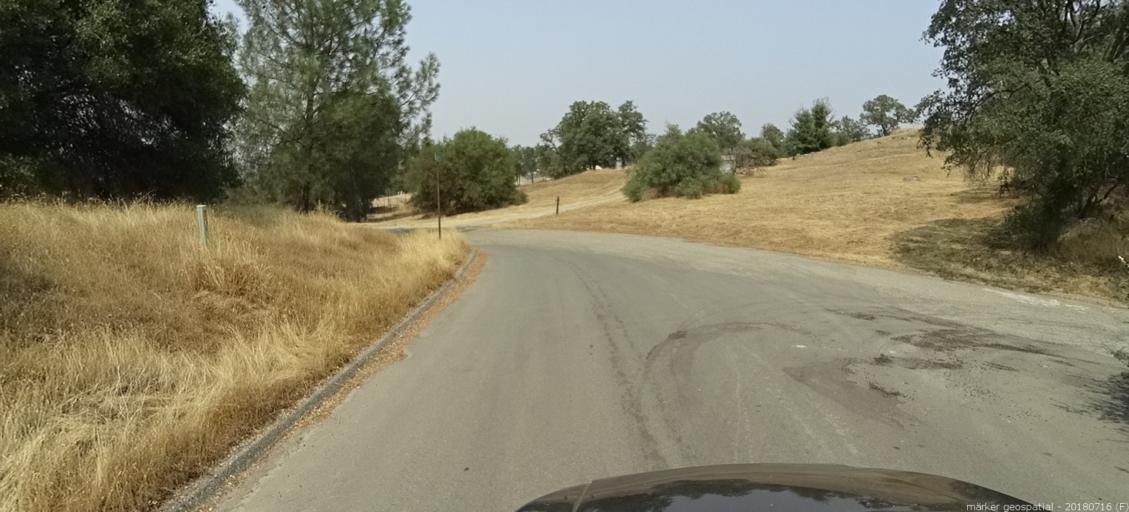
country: US
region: California
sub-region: Madera County
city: Yosemite Lakes
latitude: 37.2377
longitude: -119.7814
